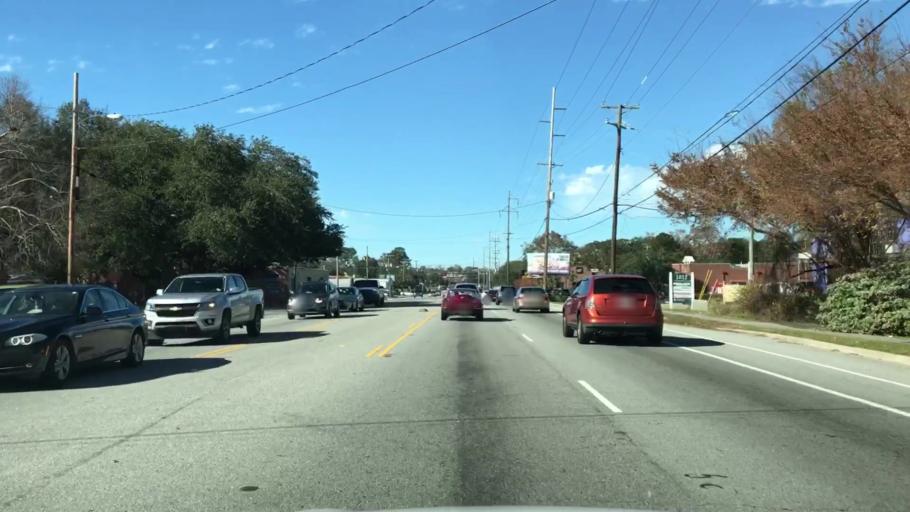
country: US
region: South Carolina
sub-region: Charleston County
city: Charleston
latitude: 32.7933
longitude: -79.9904
